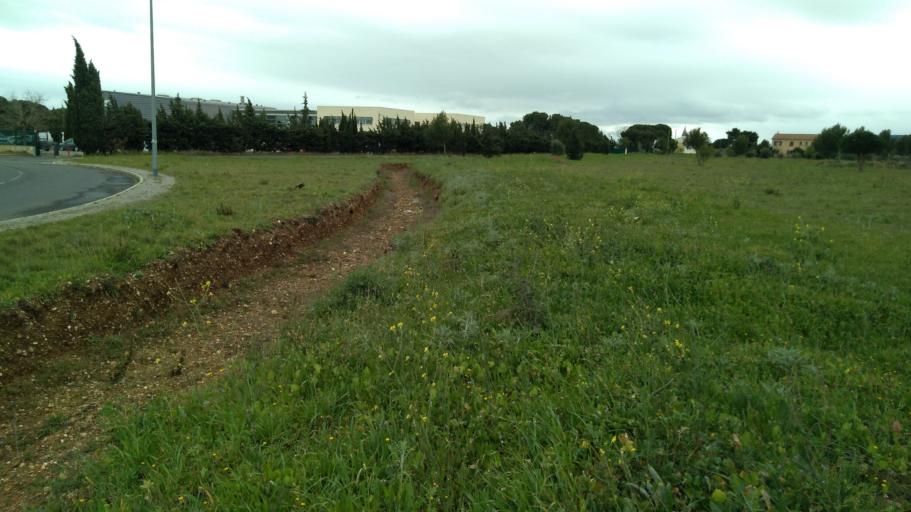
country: FR
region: Languedoc-Roussillon
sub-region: Departement de l'Aude
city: Narbonne
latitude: 43.1578
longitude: 2.9940
